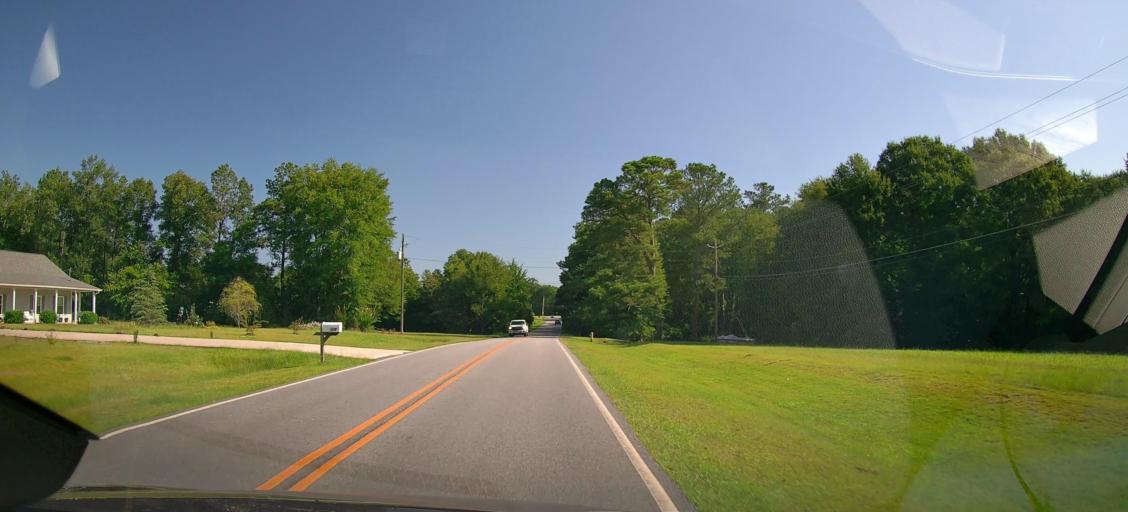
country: US
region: Georgia
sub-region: Peach County
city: Byron
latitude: 32.7410
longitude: -83.7050
